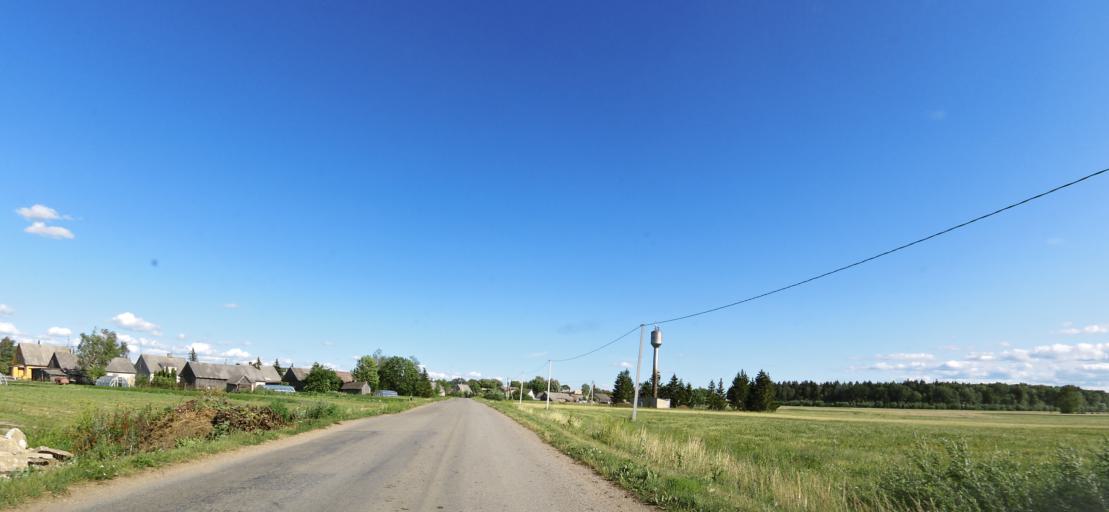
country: LT
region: Panevezys
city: Pasvalys
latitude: 56.1594
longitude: 24.4369
